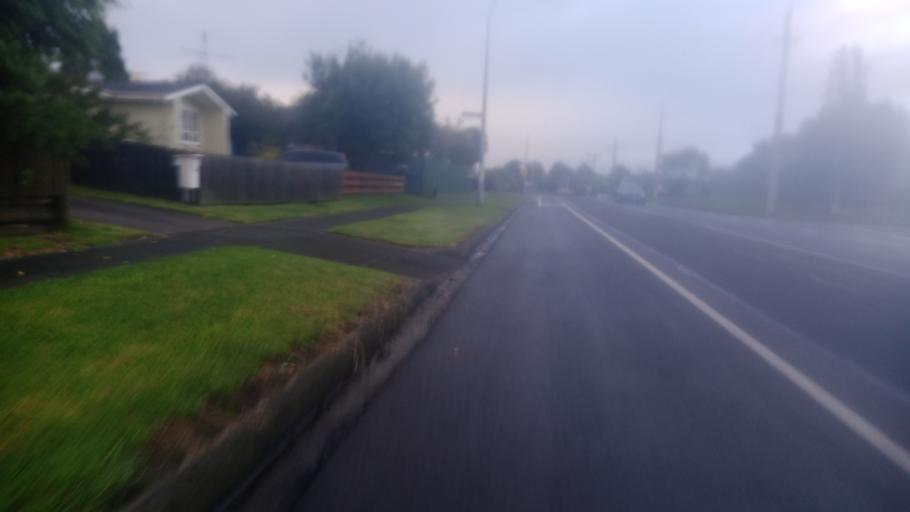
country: NZ
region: Gisborne
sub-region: Gisborne District
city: Gisborne
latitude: -38.6615
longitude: 177.9936
